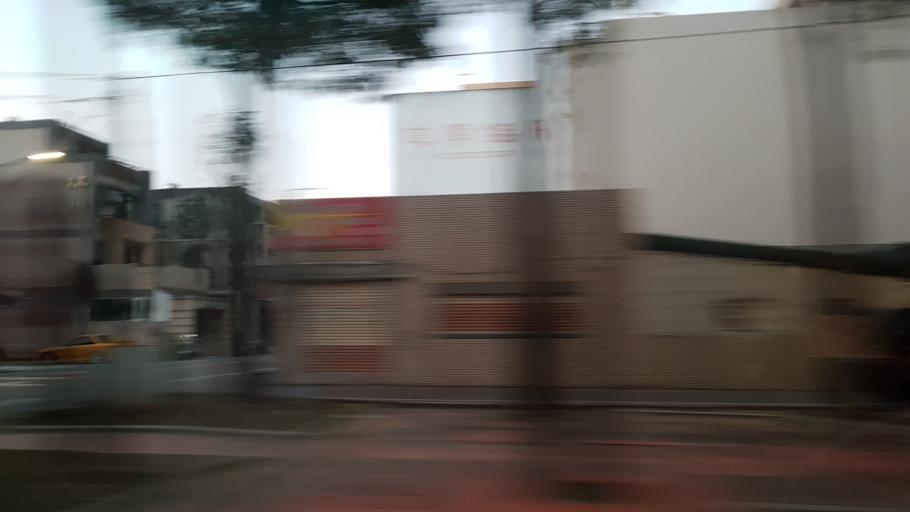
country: TW
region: Taiwan
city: Xinying
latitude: 23.3082
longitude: 120.2980
